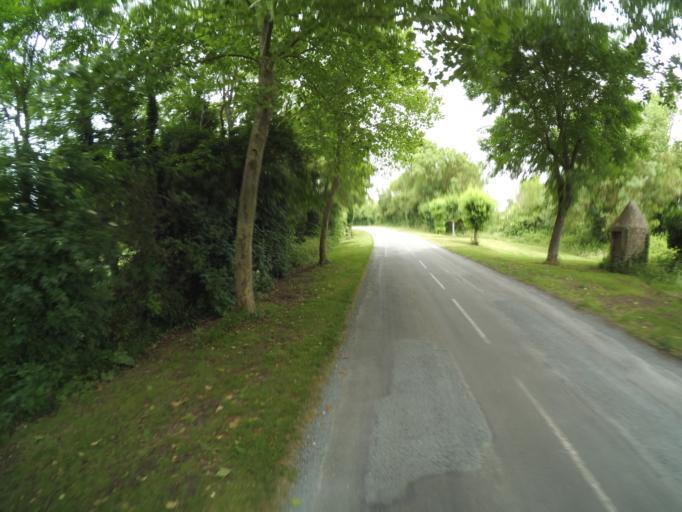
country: FR
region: Poitou-Charentes
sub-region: Departement de la Charente-Maritime
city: Saint-Laurent-de-la-Pree
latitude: 45.9832
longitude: -1.0053
